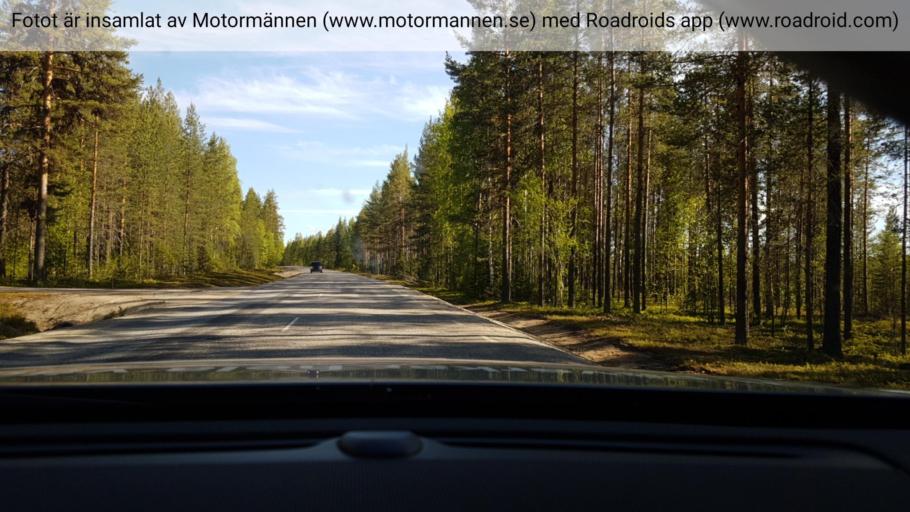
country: SE
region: Vaesterbotten
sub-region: Norsjo Kommun
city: Norsjoe
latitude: 64.6170
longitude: 19.2892
